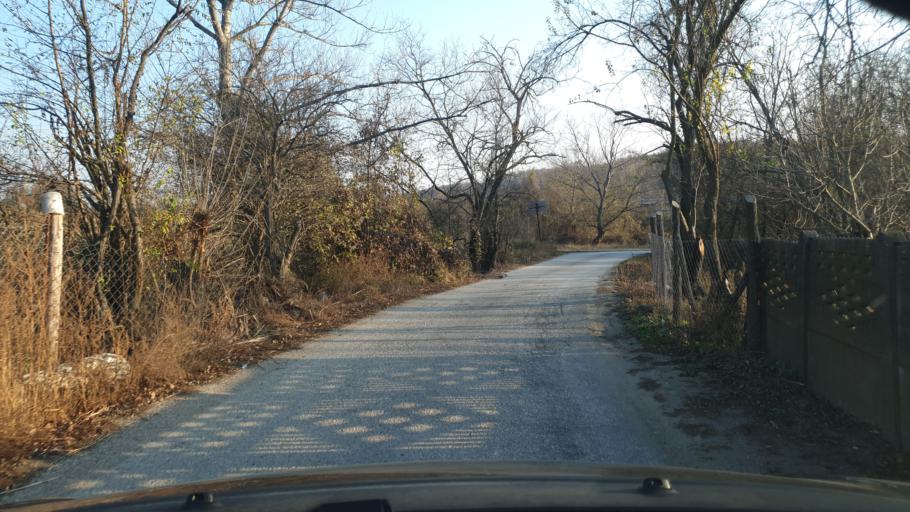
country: RS
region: Central Serbia
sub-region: Zajecarski Okrug
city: Zajecar
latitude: 44.0312
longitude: 22.3288
